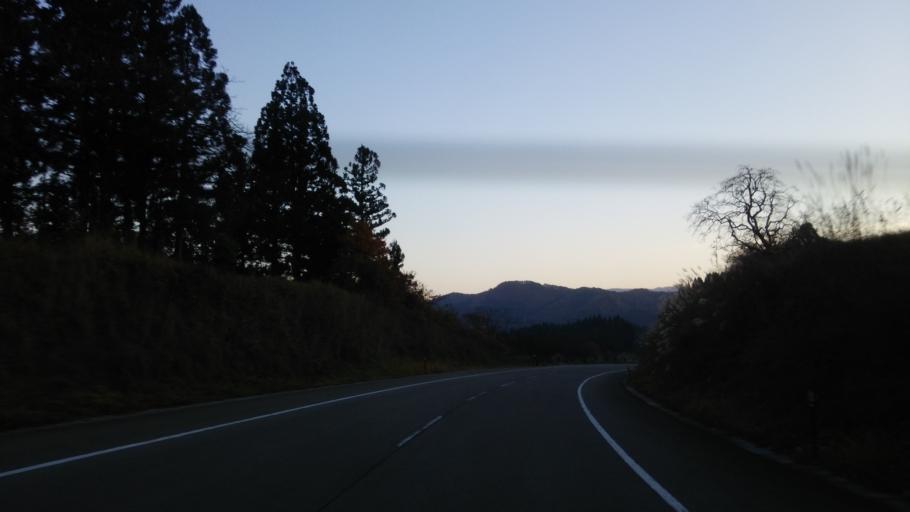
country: JP
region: Fukushima
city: Kitakata
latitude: 37.4938
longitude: 139.6636
